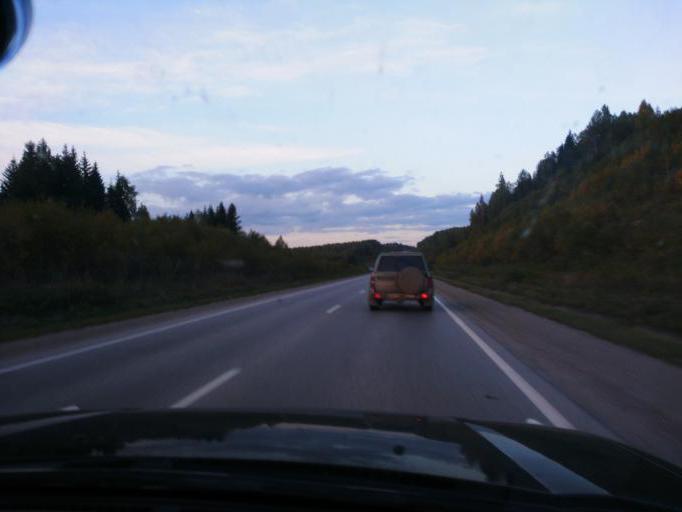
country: RU
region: Perm
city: Polazna
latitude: 58.2934
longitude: 56.5181
